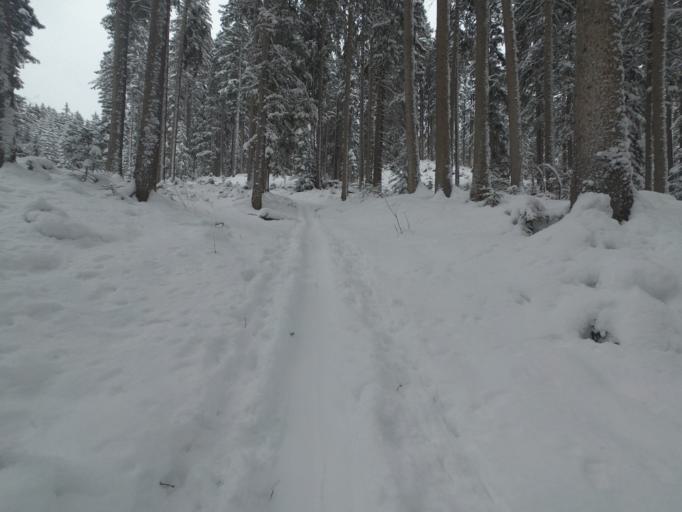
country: AT
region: Salzburg
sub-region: Politischer Bezirk Sankt Johann im Pongau
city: Wagrain
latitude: 47.3215
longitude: 13.2775
